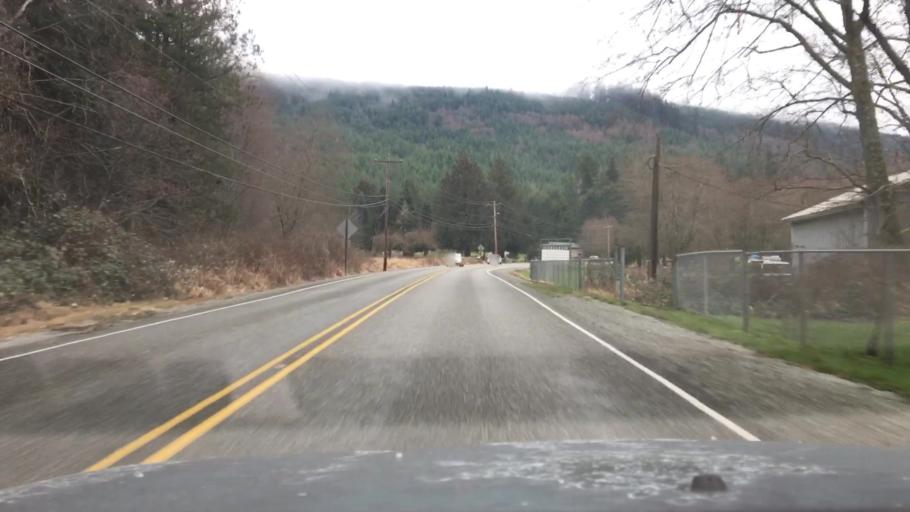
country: US
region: Washington
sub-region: Whatcom County
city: Sudden Valley
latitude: 48.6392
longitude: -122.3133
